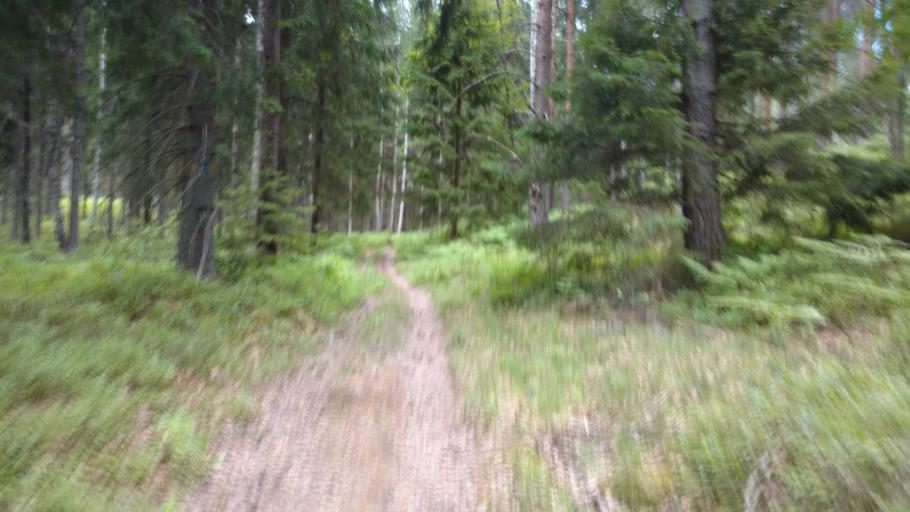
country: FI
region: Uusimaa
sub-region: Raaseporin
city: Pohja
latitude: 60.1189
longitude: 23.5591
